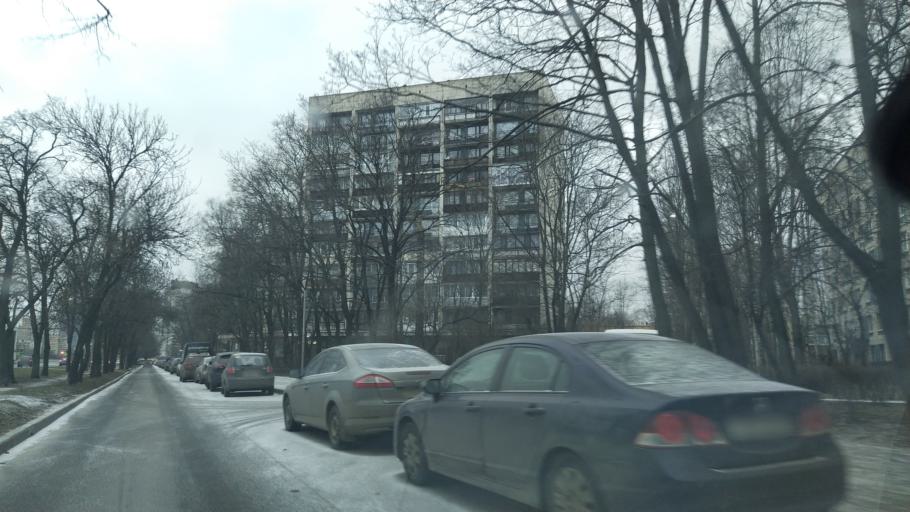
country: RU
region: St.-Petersburg
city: Kupchino
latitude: 59.8398
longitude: 30.3284
